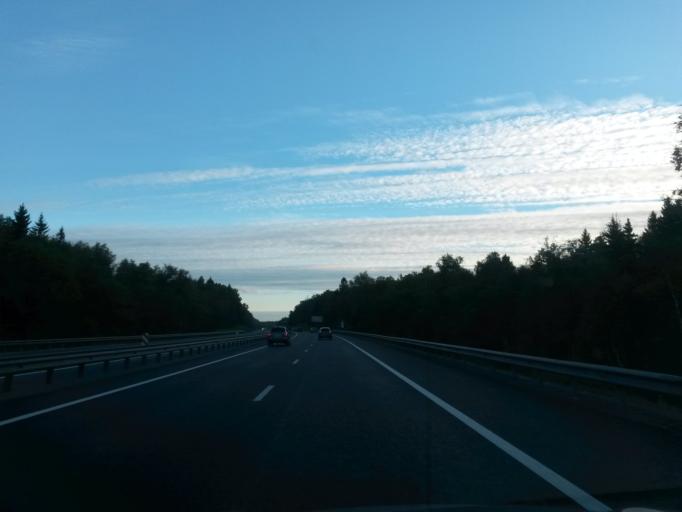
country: RU
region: Moskovskaya
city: Krasnozavodsk
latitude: 56.4387
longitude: 38.3466
